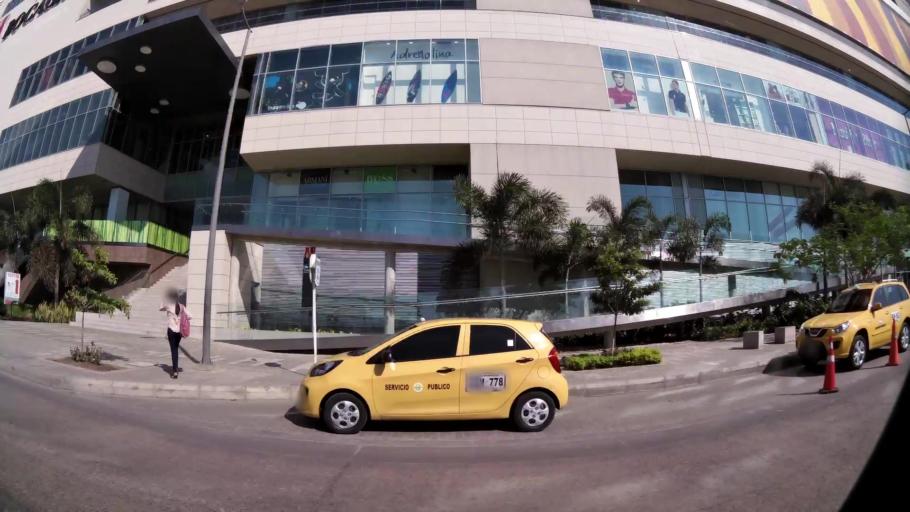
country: CO
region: Bolivar
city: Cartagena
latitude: 10.4111
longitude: -75.5515
